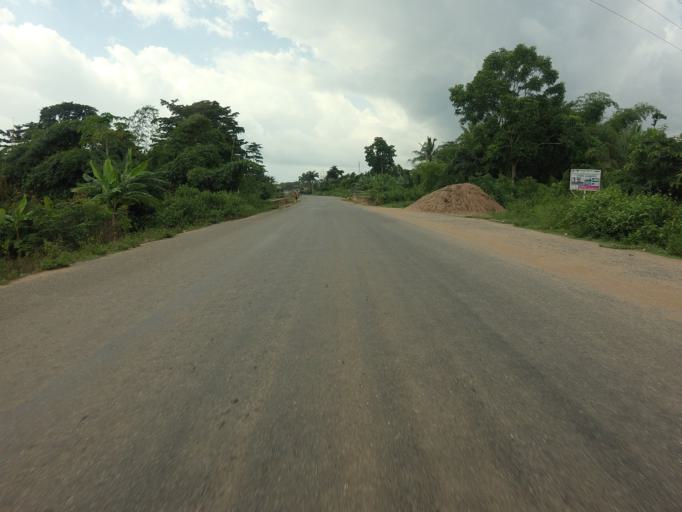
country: GH
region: Volta
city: Kpandu
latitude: 6.8965
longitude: 0.4323
